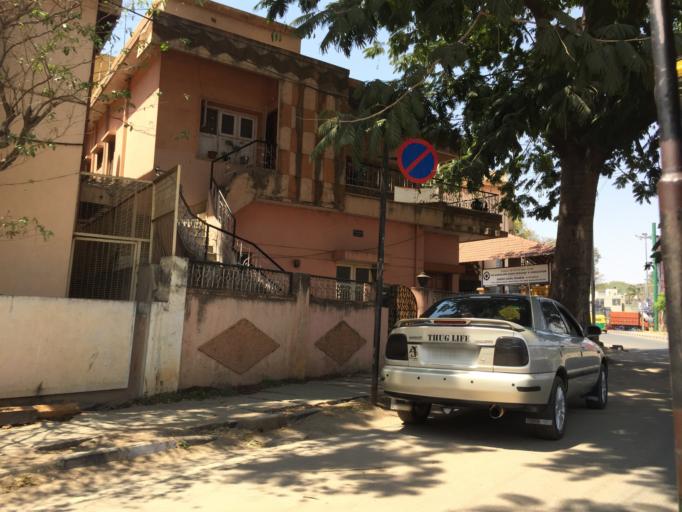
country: IN
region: Karnataka
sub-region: Bangalore Urban
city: Bangalore
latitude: 12.9951
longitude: 77.6175
